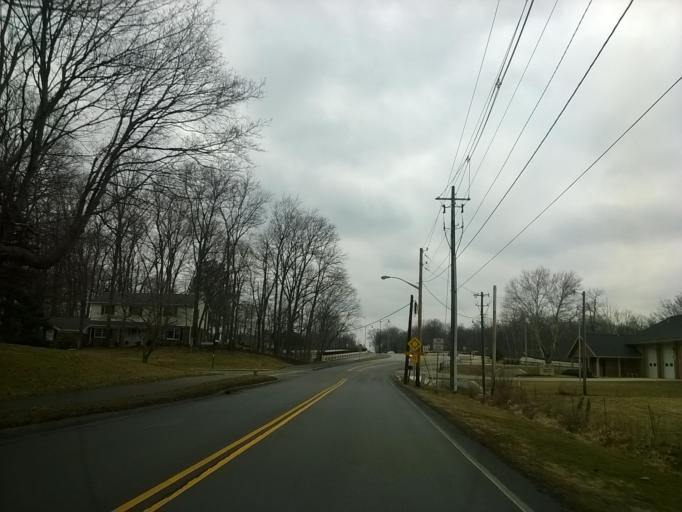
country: US
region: Indiana
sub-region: Hamilton County
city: Carmel
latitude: 39.9415
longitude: -86.1101
